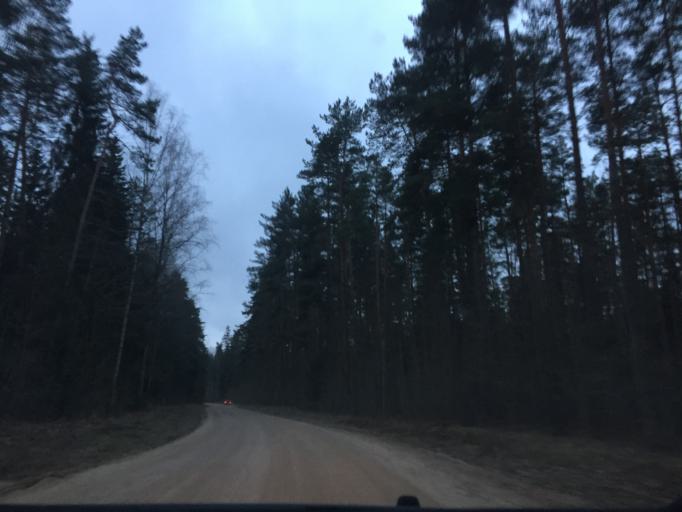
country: LV
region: Cesu Rajons
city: Cesis
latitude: 57.3476
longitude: 25.2579
